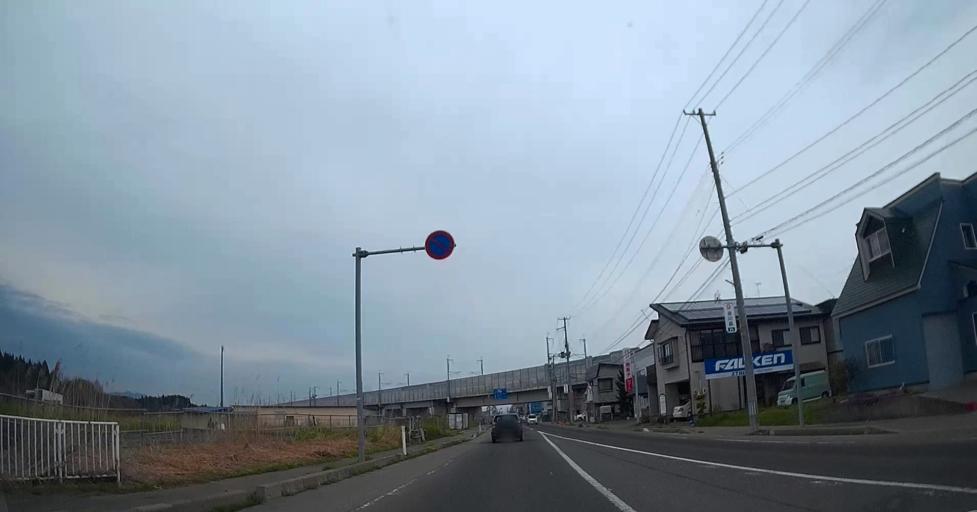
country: JP
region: Aomori
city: Aomori Shi
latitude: 40.8521
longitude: 140.6815
